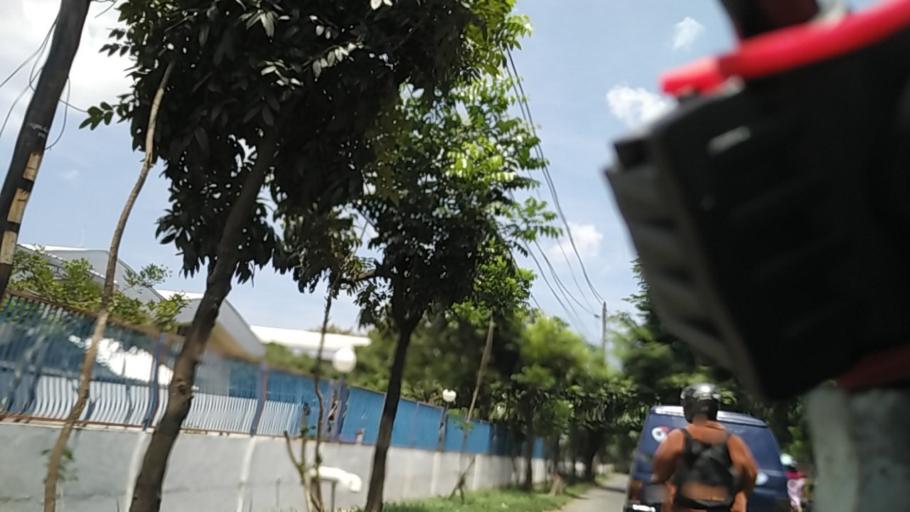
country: ID
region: Central Java
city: Semarang
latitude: -7.0038
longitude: 110.3918
